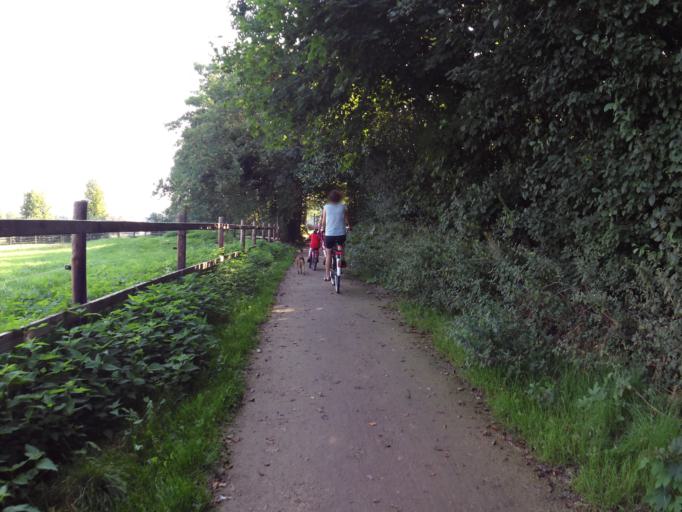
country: DE
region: North Rhine-Westphalia
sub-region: Regierungsbezirk Munster
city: Havixbeck
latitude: 51.9733
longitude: 7.4408
